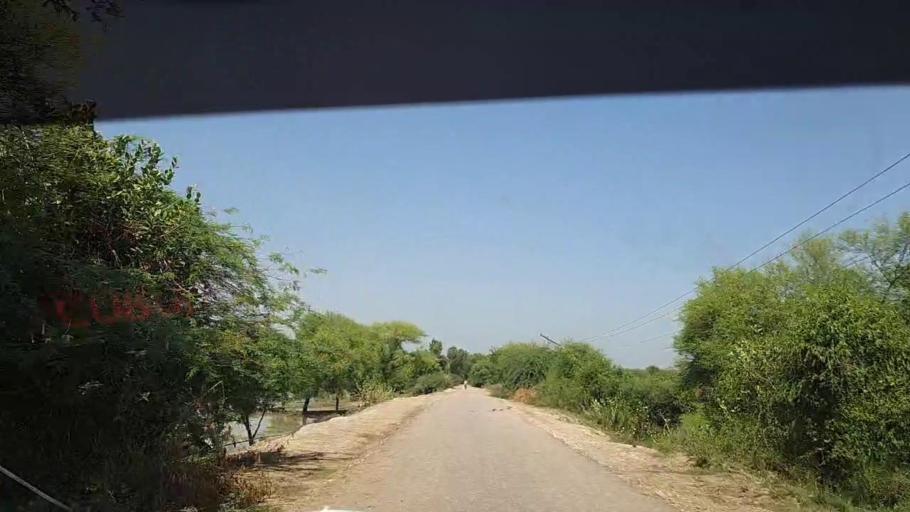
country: PK
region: Sindh
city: Ghauspur
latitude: 28.1656
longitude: 69.1396
